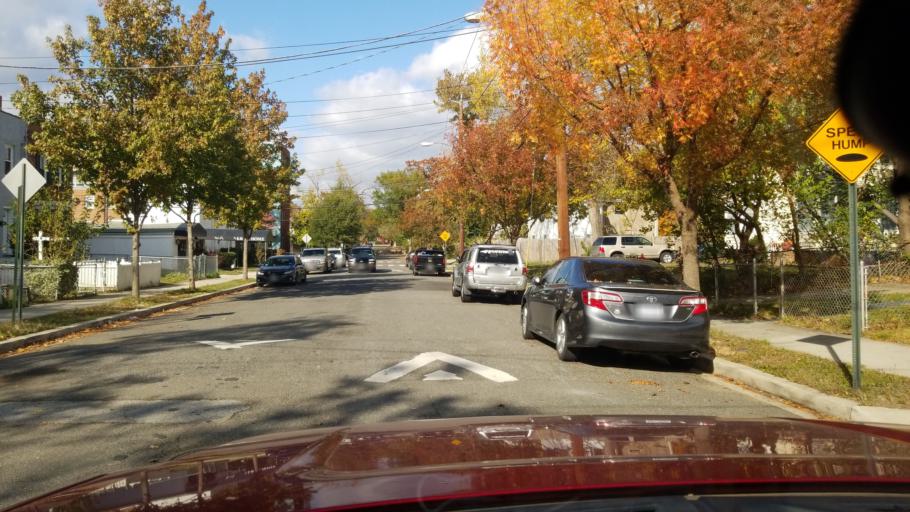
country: US
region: Maryland
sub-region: Prince George's County
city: Fairmount Heights
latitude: 38.8950
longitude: -76.9192
